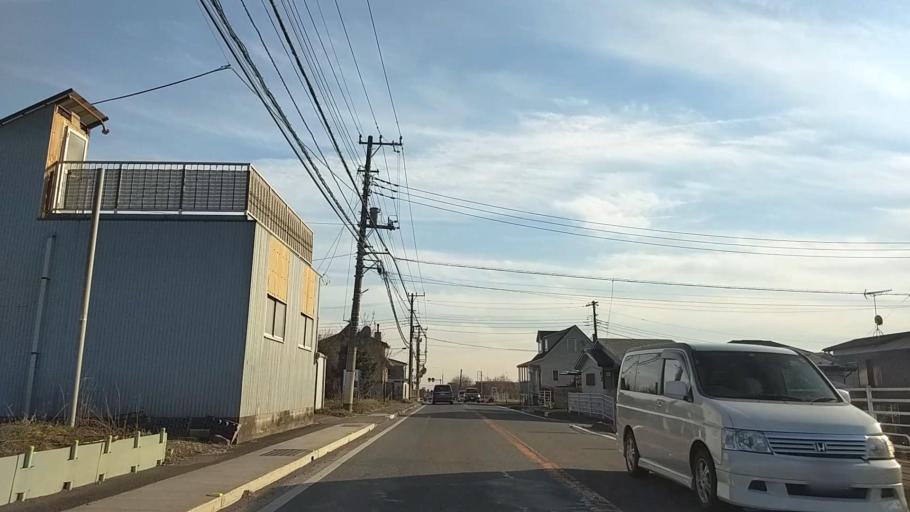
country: JP
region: Kanagawa
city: Zama
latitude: 35.5040
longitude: 139.3103
